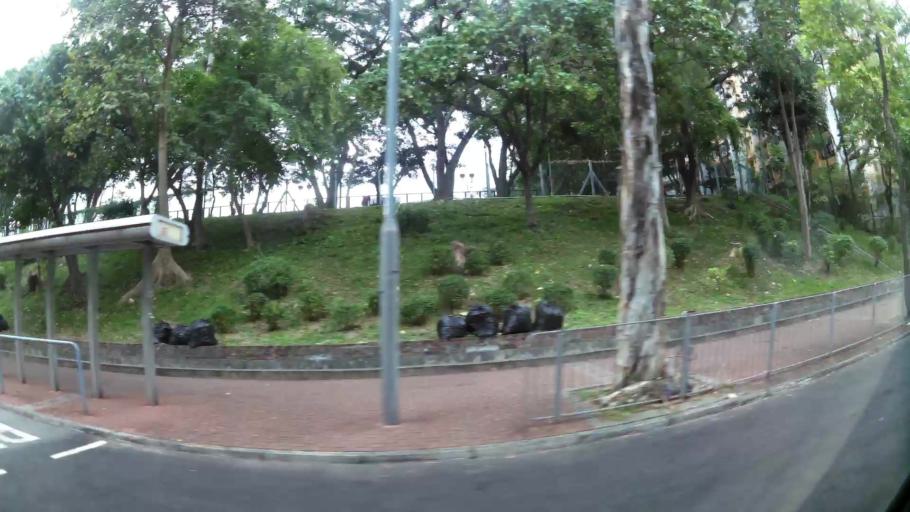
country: HK
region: Wong Tai Sin
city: Wong Tai Sin
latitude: 22.3379
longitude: 114.1927
